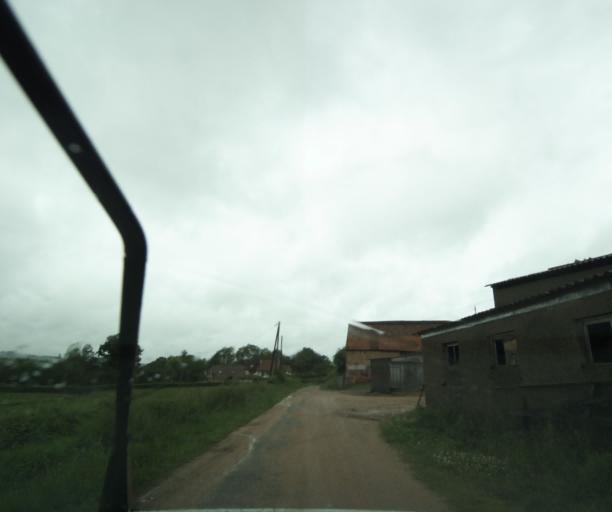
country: FR
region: Bourgogne
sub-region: Departement de Saone-et-Loire
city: Saint-Vallier
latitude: 46.4895
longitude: 4.4691
